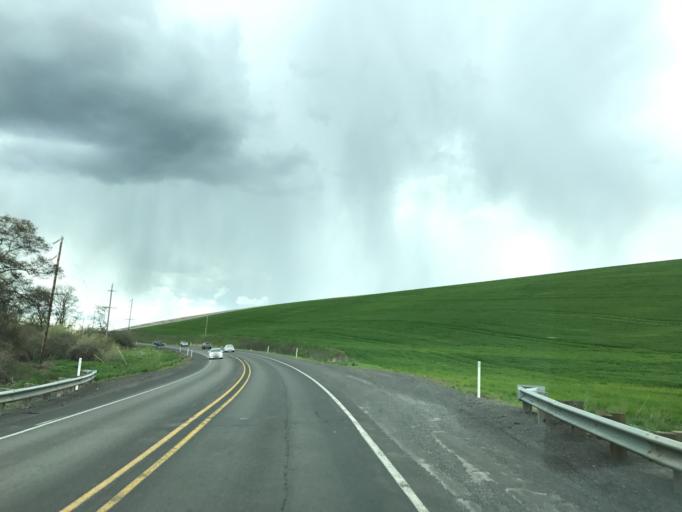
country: US
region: Washington
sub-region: Walla Walla County
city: Waitsburg
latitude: 46.1367
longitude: -118.1668
